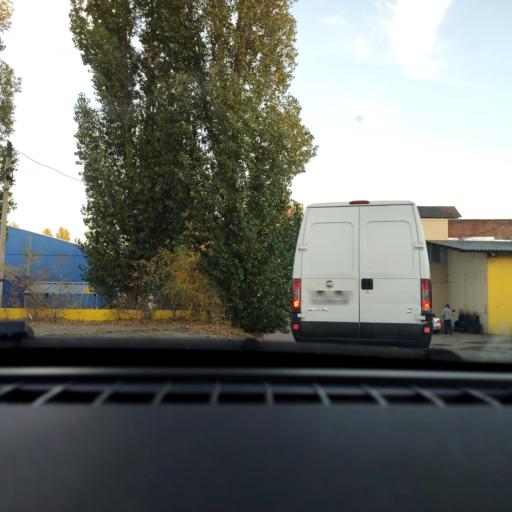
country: RU
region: Voronezj
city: Maslovka
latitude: 51.6399
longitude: 39.2815
